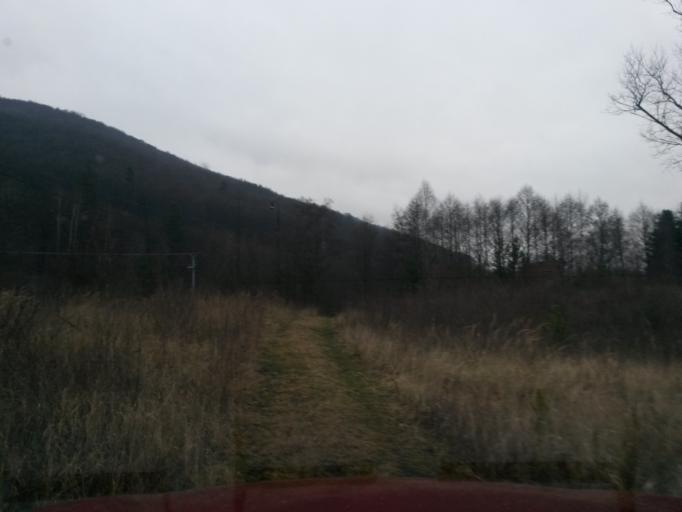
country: SK
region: Kosicky
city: Dobsina
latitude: 48.7405
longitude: 20.4192
